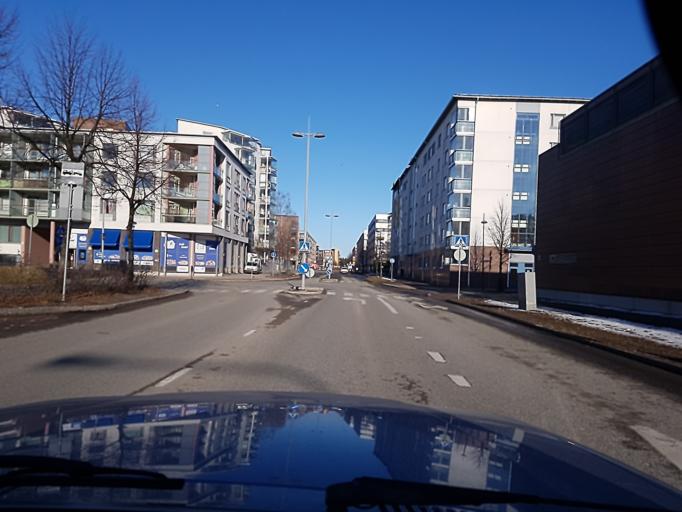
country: FI
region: Uusimaa
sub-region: Helsinki
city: Vantaa
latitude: 60.2038
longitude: 25.1454
